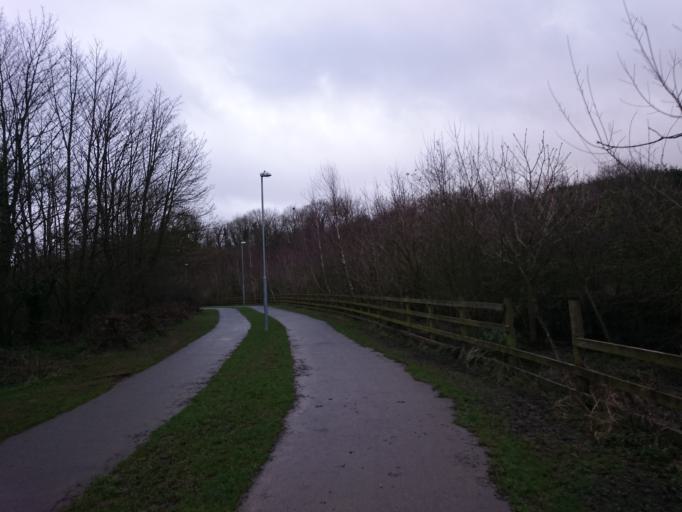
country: IE
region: Leinster
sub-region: Kilkenny
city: Kilkenny
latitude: 52.6689
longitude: -7.2620
